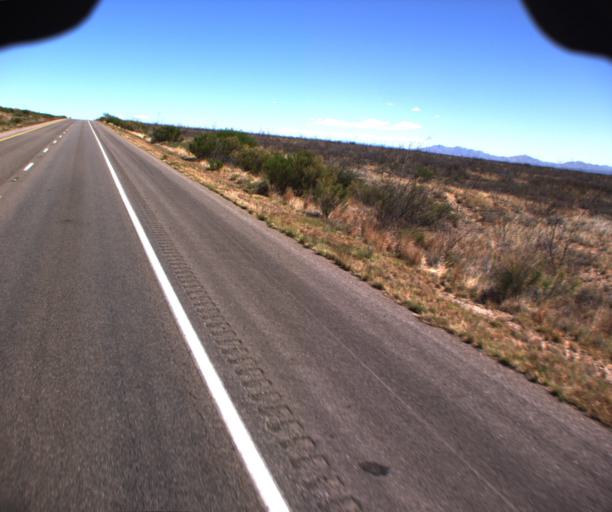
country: US
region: Arizona
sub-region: Cochise County
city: Whetstone
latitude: 31.7945
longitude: -110.3499
